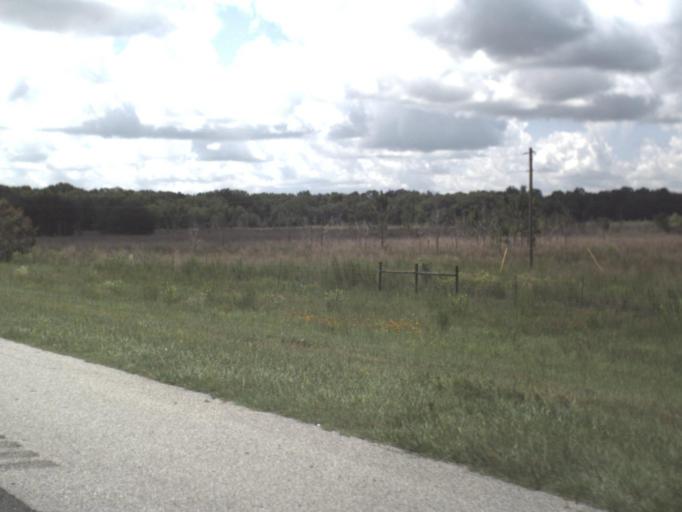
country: US
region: Florida
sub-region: Suwannee County
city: Wellborn
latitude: 30.3246
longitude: -82.8151
